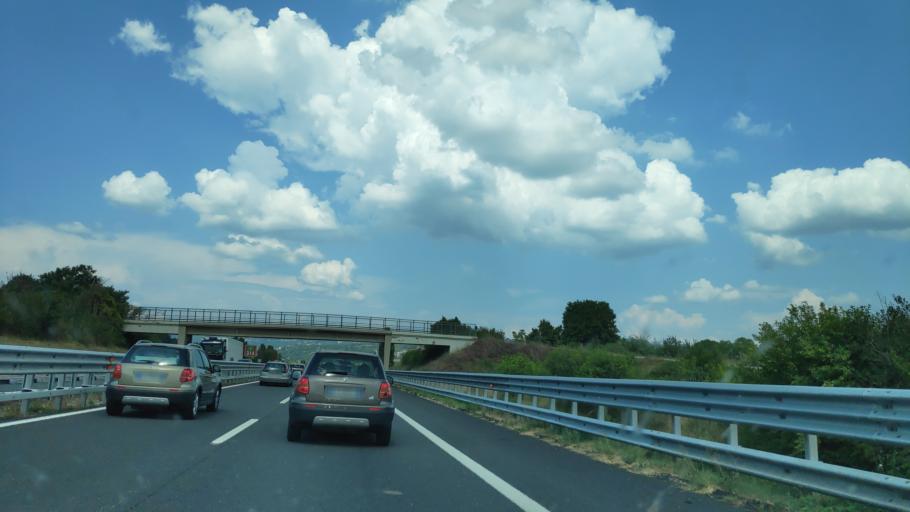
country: IT
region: Umbria
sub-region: Provincia di Terni
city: Fabro Scalo
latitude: 42.8554
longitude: 12.0379
